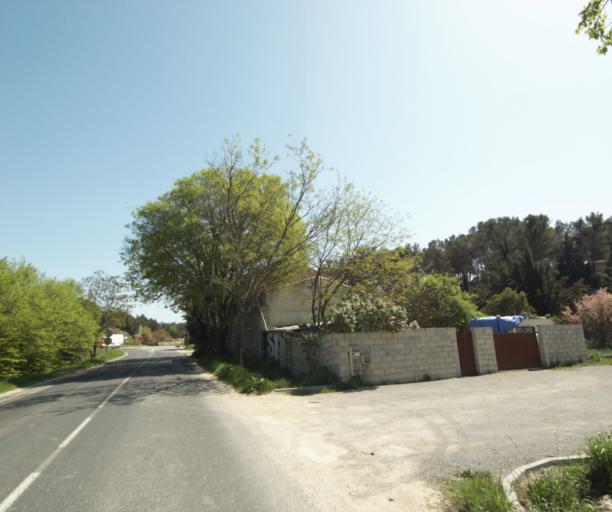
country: FR
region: Languedoc-Roussillon
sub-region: Departement de l'Herault
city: Montferrier-sur-Lez
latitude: 43.6550
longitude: 3.8339
